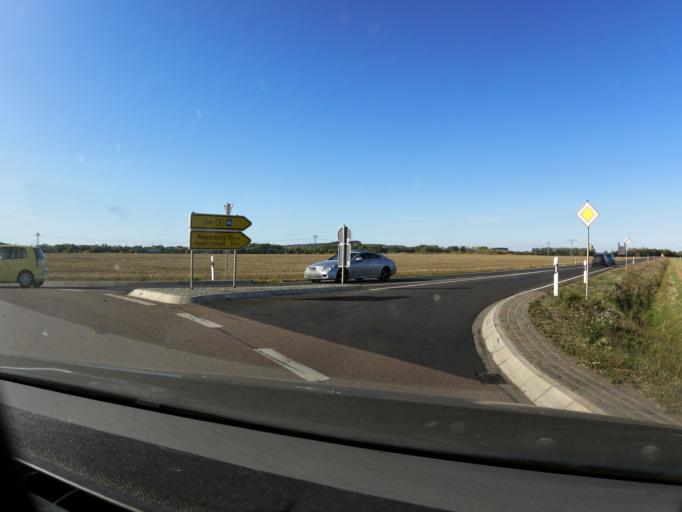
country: DE
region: Saxony-Anhalt
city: Quedlinburg
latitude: 51.7907
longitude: 11.1834
